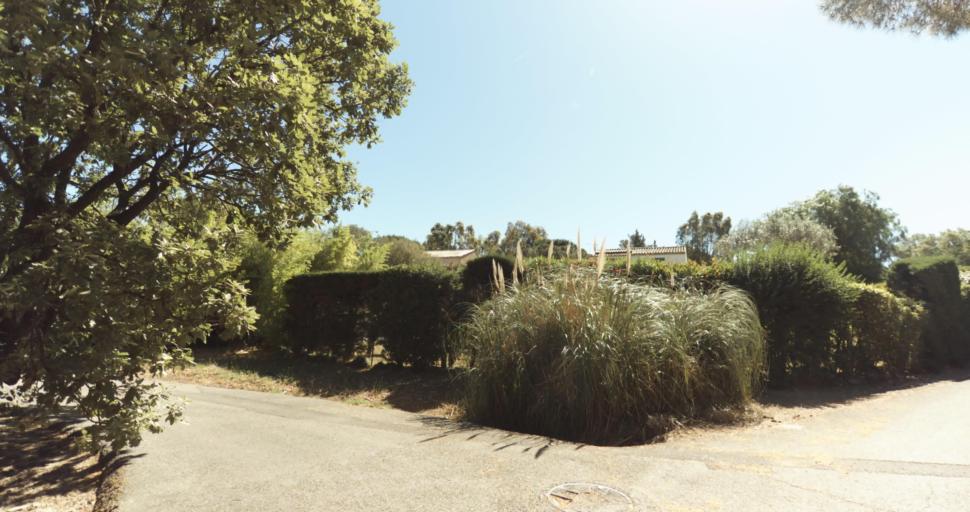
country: FR
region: Provence-Alpes-Cote d'Azur
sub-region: Departement du Var
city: Gassin
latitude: 43.2557
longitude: 6.5989
